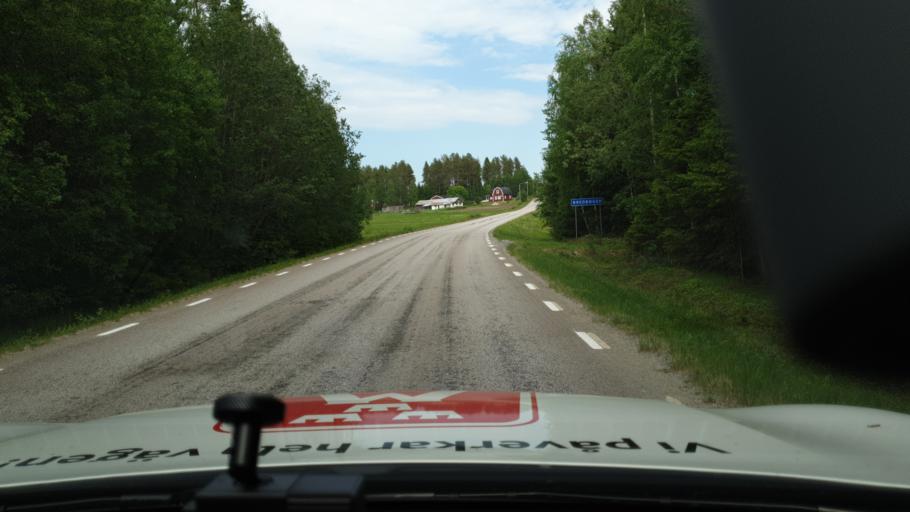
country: SE
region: Vaesterbotten
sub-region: Umea Kommun
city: Hoernefors
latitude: 63.6131
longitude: 19.8771
